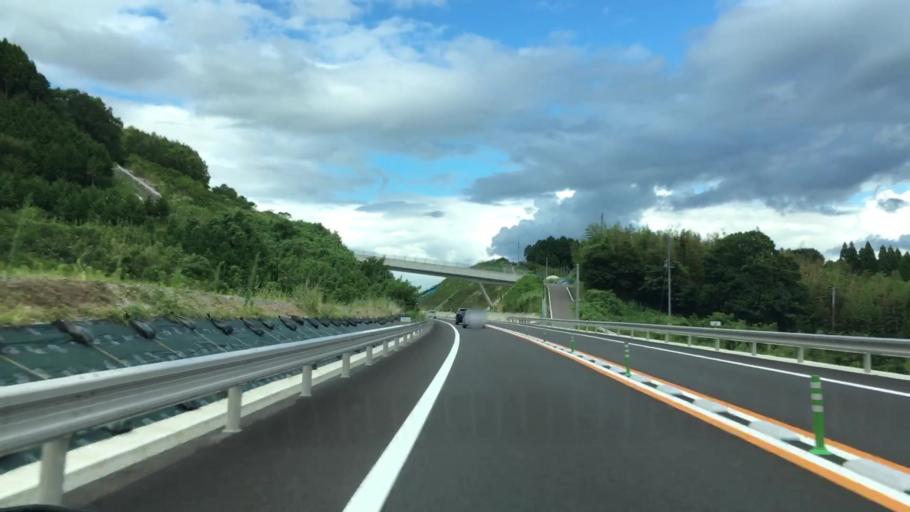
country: JP
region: Saga Prefecture
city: Imaricho-ko
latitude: 33.3198
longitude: 129.9251
